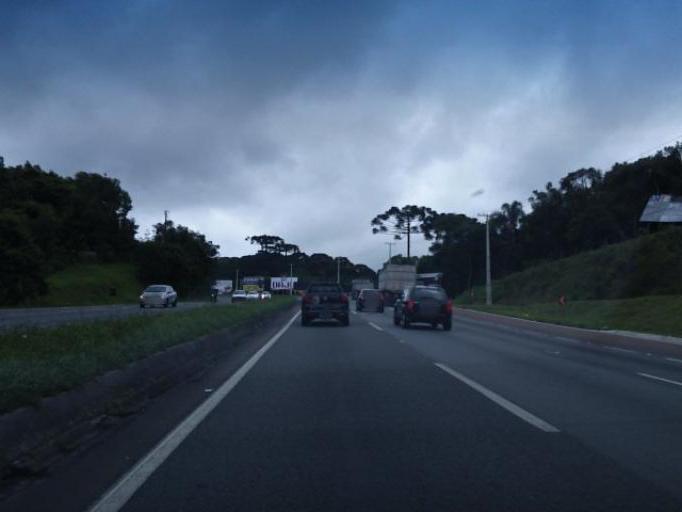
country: BR
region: Parana
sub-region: Sao Jose Dos Pinhais
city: Sao Jose dos Pinhais
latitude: -25.5916
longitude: -49.1718
